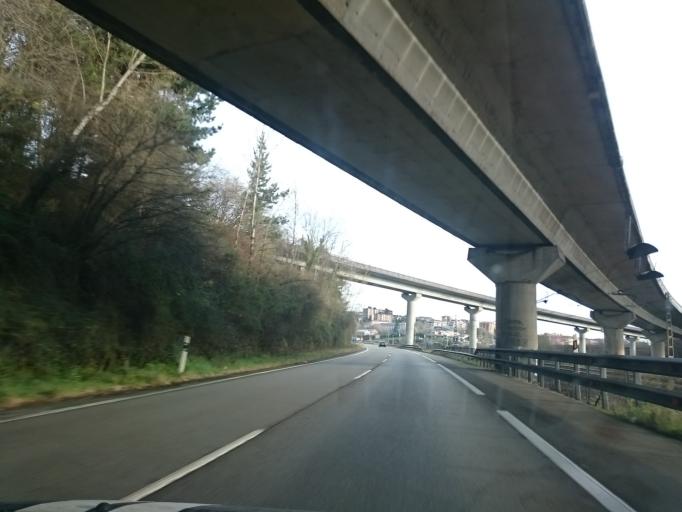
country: ES
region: Asturias
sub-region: Province of Asturias
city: Oviedo
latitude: 43.3466
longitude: -5.8604
